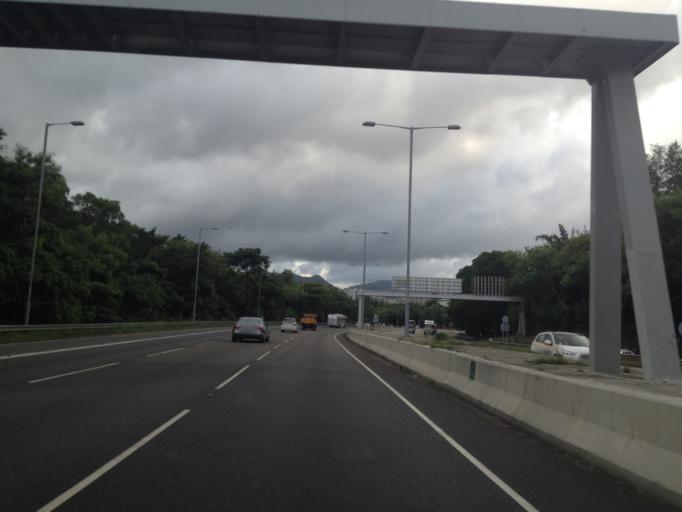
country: HK
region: Sha Tin
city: Sha Tin
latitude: 22.4100
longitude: 114.2121
